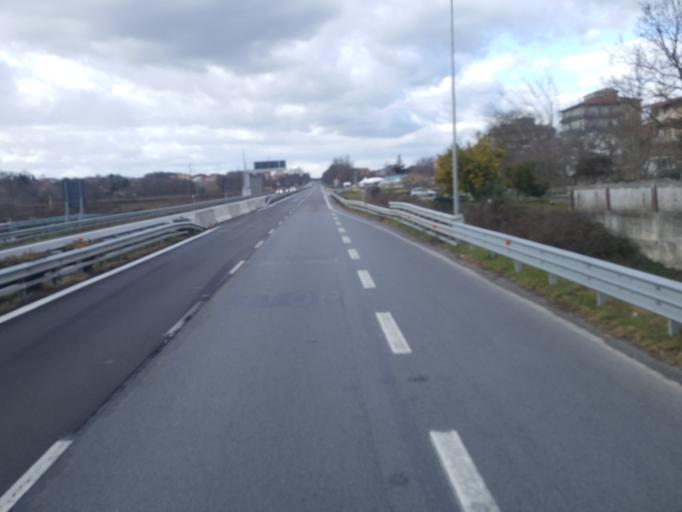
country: IT
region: Calabria
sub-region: Provincia di Cosenza
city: Santo Stefano di Rogliano
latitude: 39.2011
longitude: 16.3118
